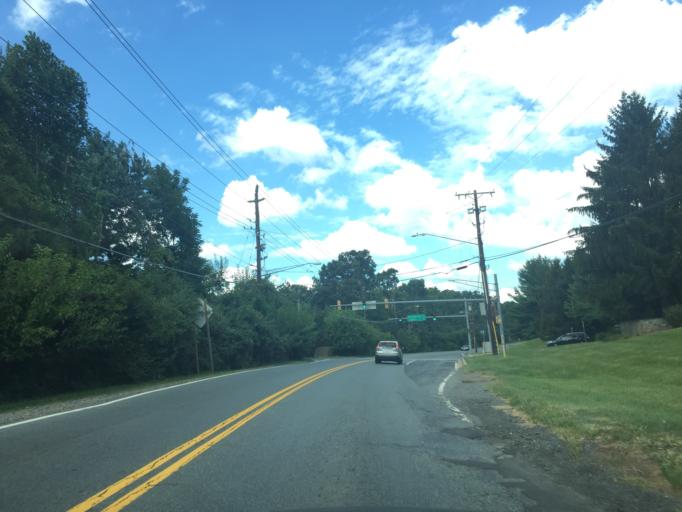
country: US
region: Maryland
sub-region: Montgomery County
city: Montgomery Village
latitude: 39.1825
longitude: -77.1816
